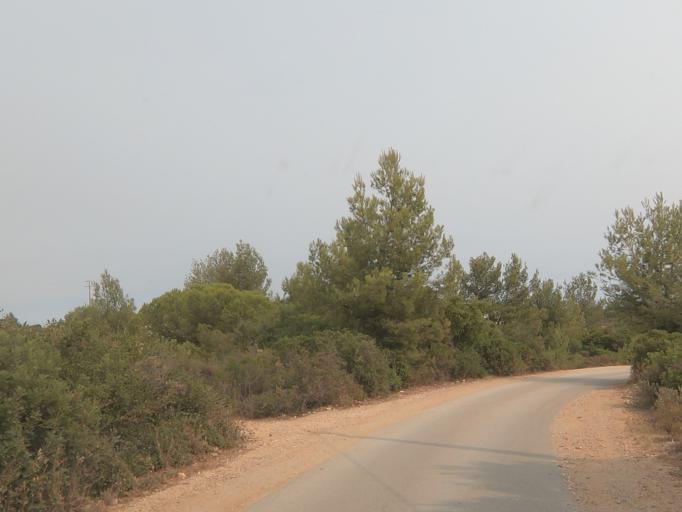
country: PT
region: Faro
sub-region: Silves
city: Armacao de Pera
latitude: 37.0943
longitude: -8.4011
